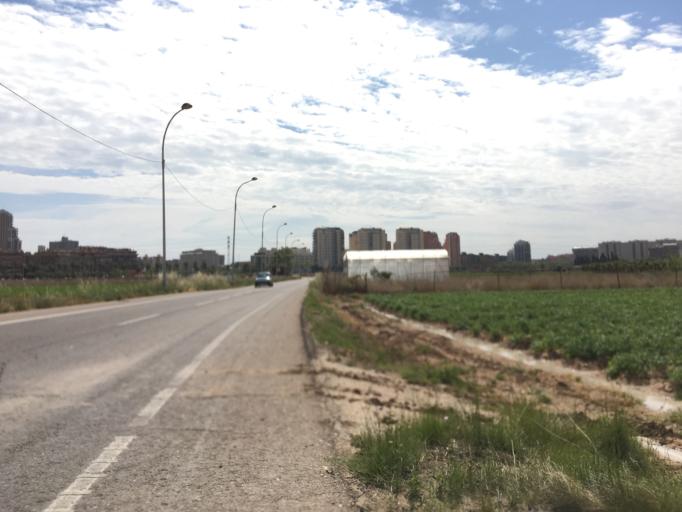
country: ES
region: Valencia
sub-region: Provincia de Valencia
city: Mislata
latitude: 39.4893
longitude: -0.4122
